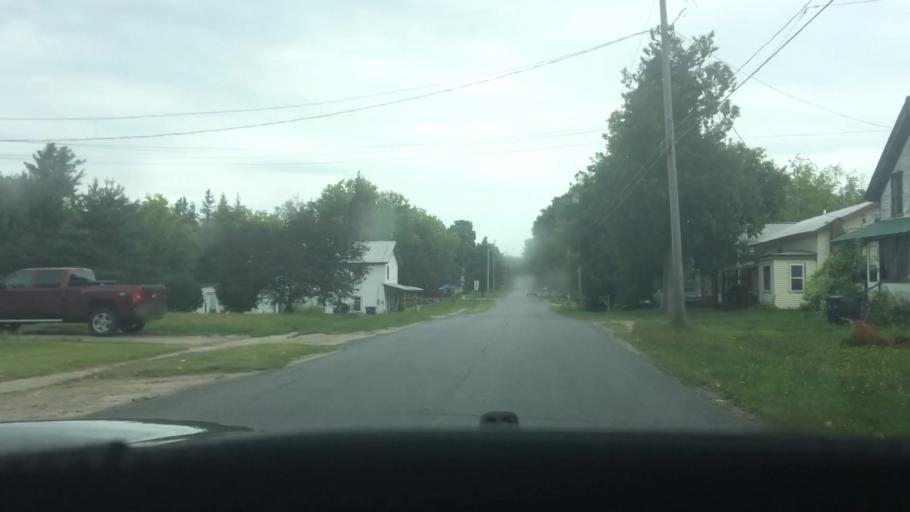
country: US
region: New York
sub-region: St. Lawrence County
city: Canton
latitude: 44.4687
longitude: -75.2303
